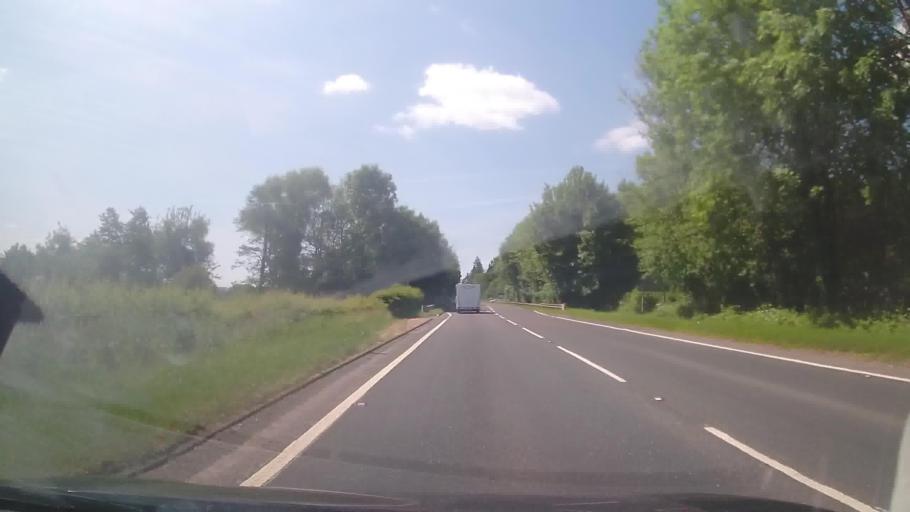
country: GB
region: England
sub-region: Shropshire
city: Ludlow
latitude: 52.3409
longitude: -2.7100
